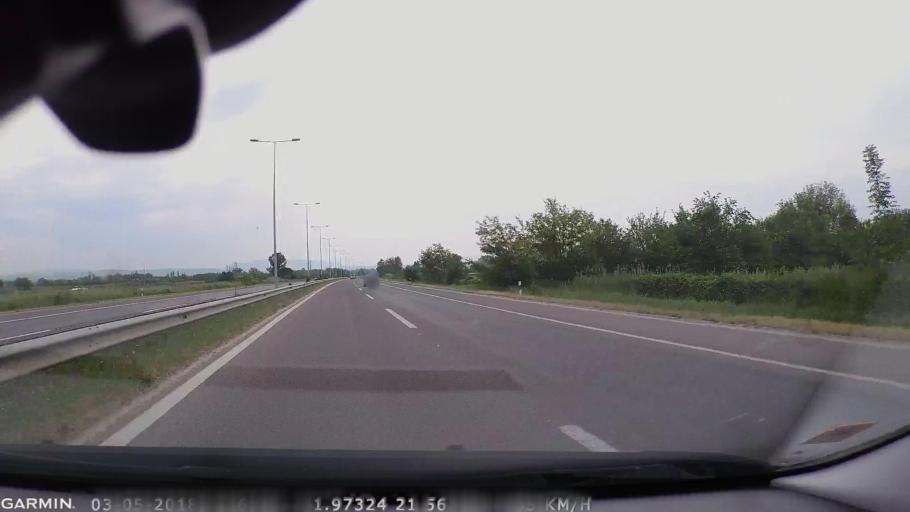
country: MK
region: Ilinden
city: Jurumleri
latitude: 41.9744
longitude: 21.5572
